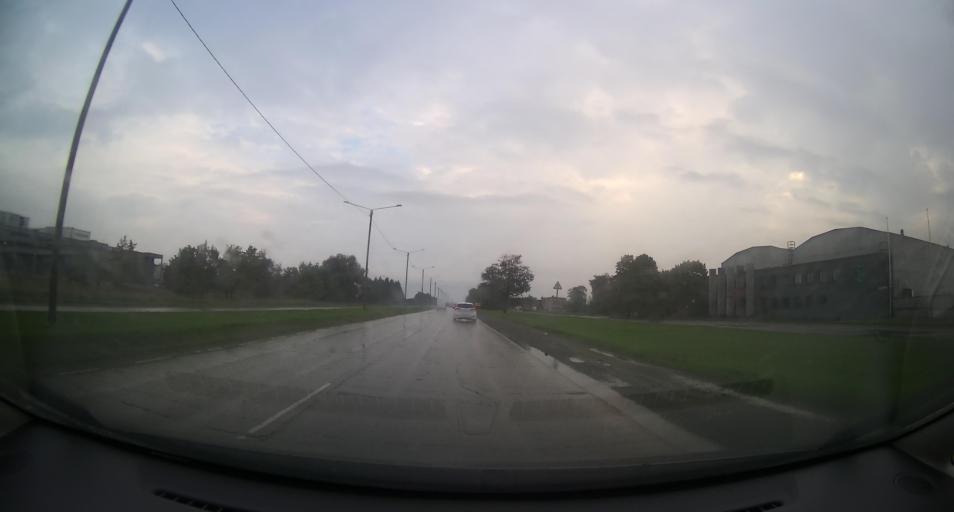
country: EE
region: Harju
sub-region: Tallinna linn
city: Kose
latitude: 59.4378
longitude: 24.8835
